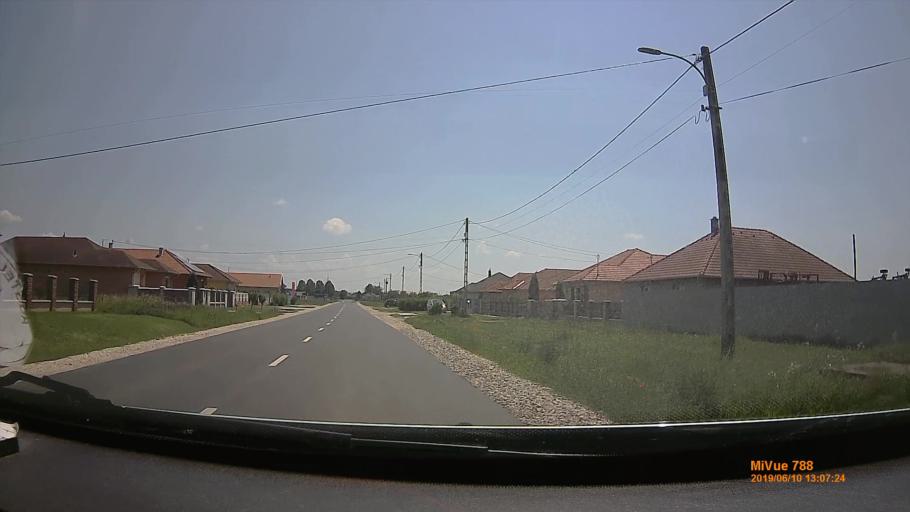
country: HU
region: Borsod-Abauj-Zemplen
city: Gesztely
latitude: 48.0876
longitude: 20.9685
